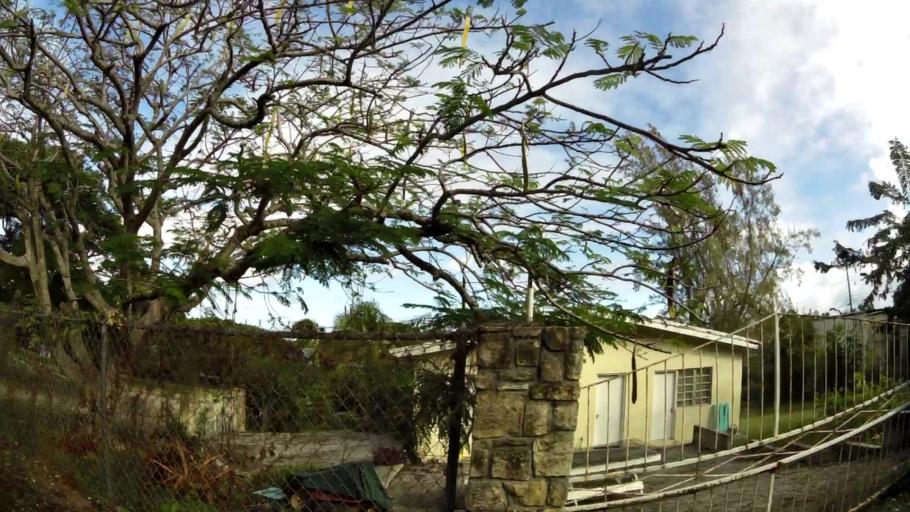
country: AG
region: Saint Peter
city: Parham
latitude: 17.0958
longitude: -61.7247
